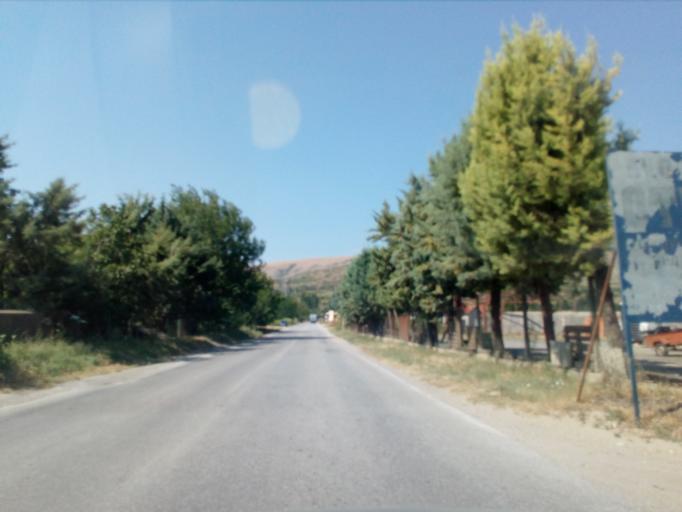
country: MK
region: Veles
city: Veles
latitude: 41.7448
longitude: 21.7648
